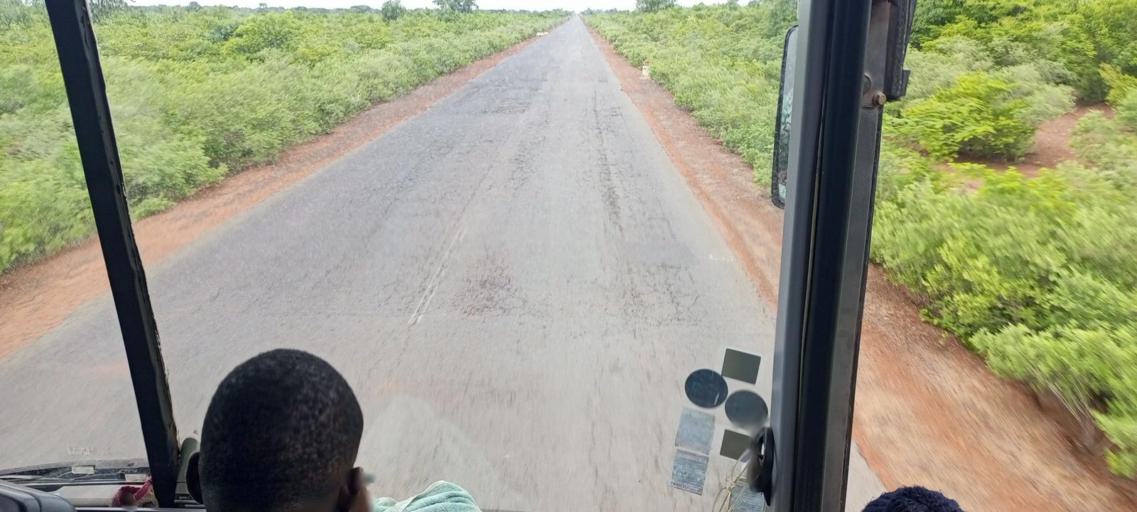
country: ML
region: Sikasso
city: Koutiala
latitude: 12.5539
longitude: -5.5872
